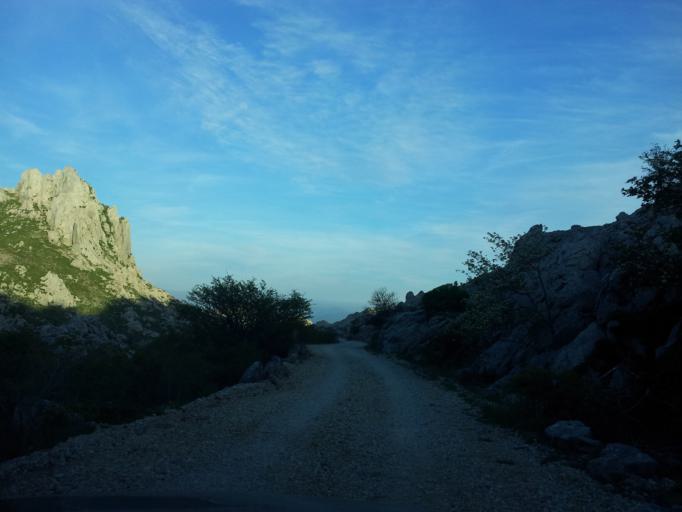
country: HR
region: Zadarska
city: Obrovac
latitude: 44.2679
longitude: 15.6401
